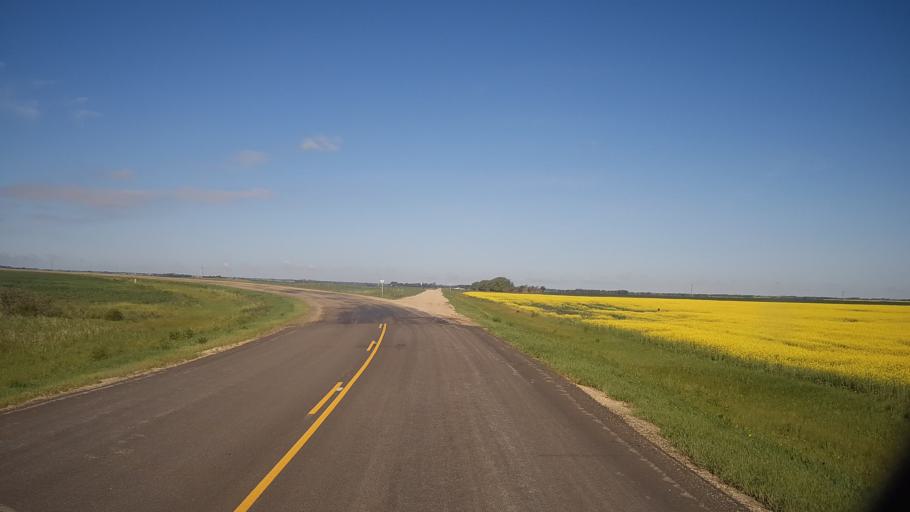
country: CA
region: Saskatchewan
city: Watrous
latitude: 51.8235
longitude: -105.2809
